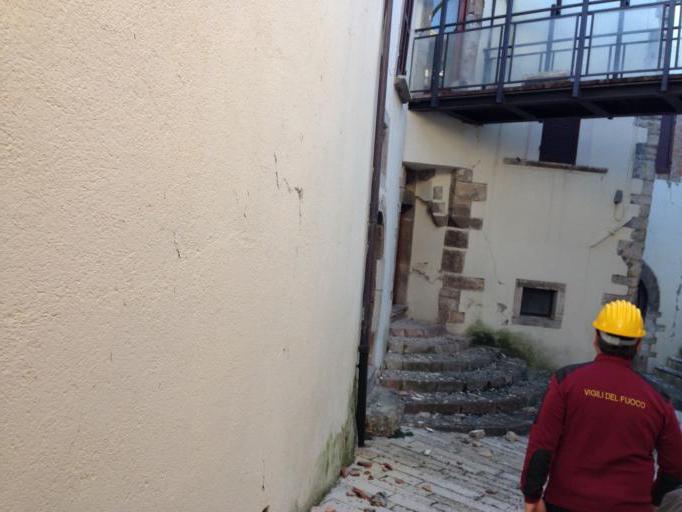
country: IT
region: Umbria
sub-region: Provincia di Perugia
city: Preci
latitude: 42.8785
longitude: 13.0392
